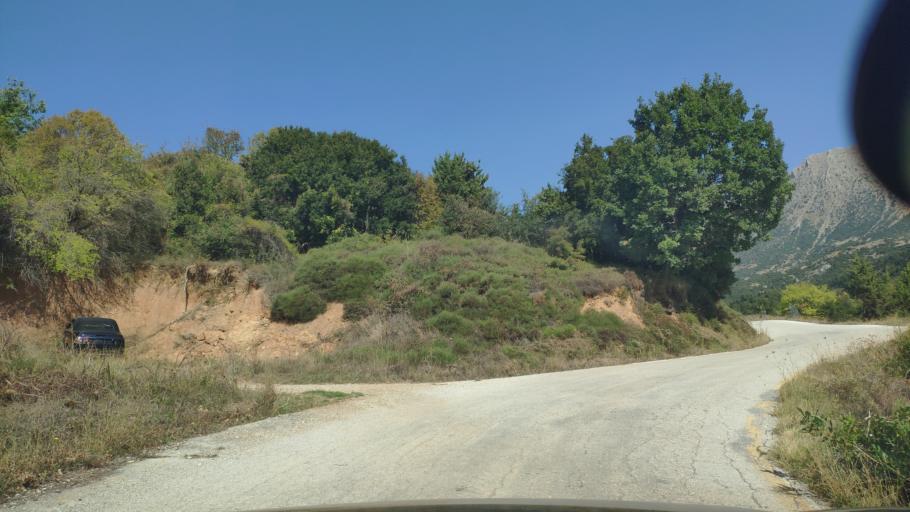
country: GR
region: Peloponnese
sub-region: Nomos Korinthias
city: Nemea
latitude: 37.8669
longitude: 22.3872
